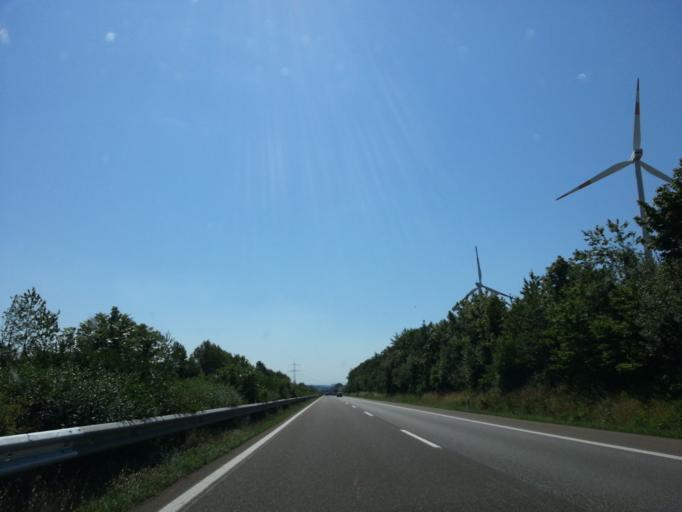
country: DE
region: Rheinland-Pfalz
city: Heilenbach
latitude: 50.0669
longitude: 6.4746
